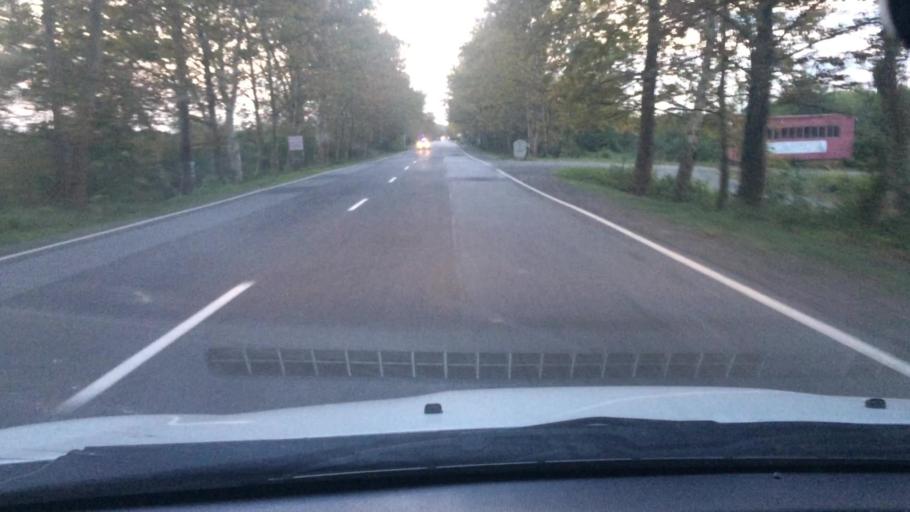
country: GE
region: Guria
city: Urek'i
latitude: 42.0143
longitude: 41.7733
